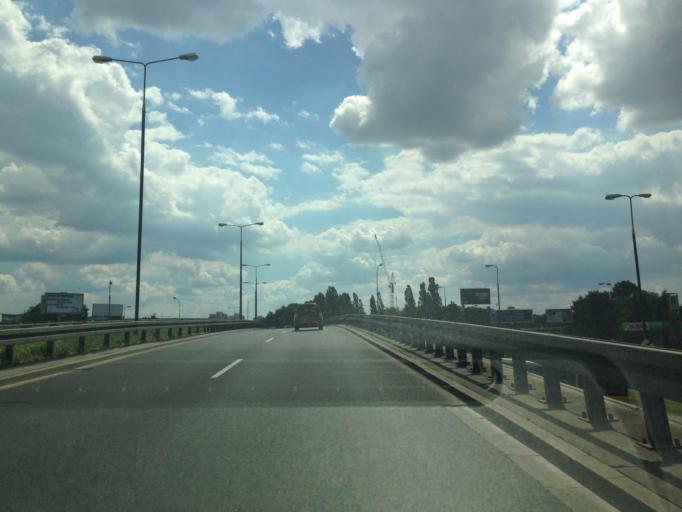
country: PL
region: Masovian Voivodeship
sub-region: Warszawa
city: Wola
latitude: 52.2389
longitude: 20.9563
